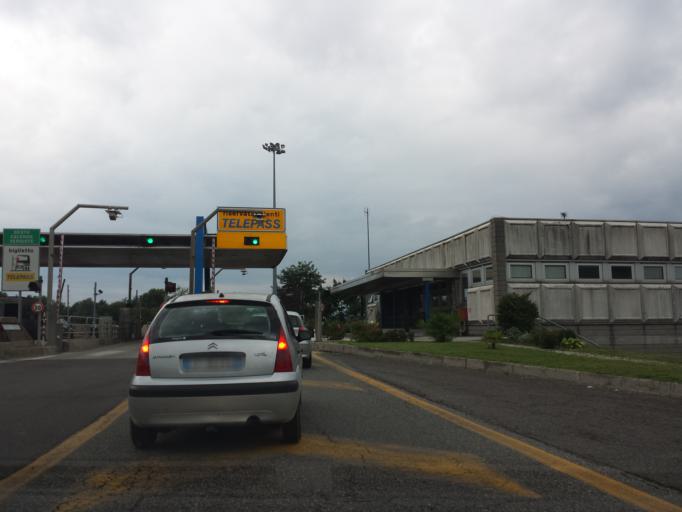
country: IT
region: Lombardy
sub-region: Provincia di Varese
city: Vergiate
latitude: 45.7210
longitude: 8.6710
